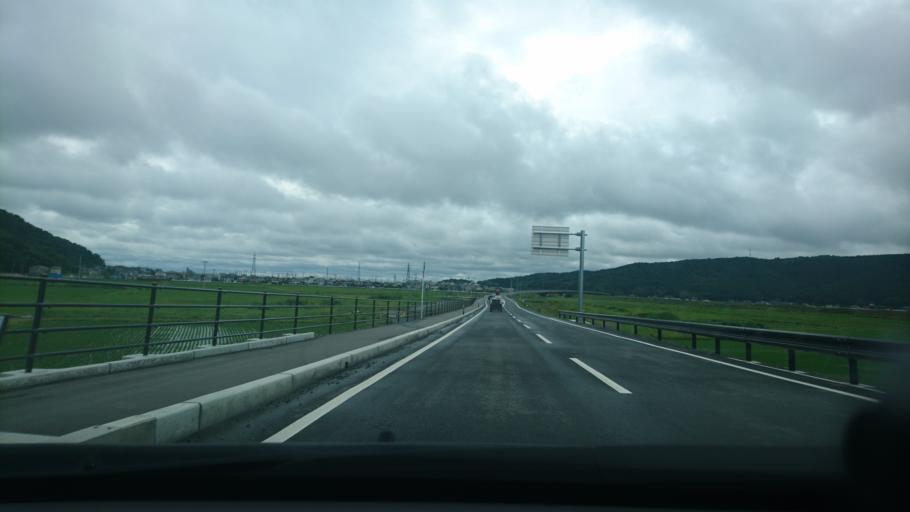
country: JP
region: Miyagi
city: Ishinomaki
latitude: 38.4487
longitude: 141.3457
